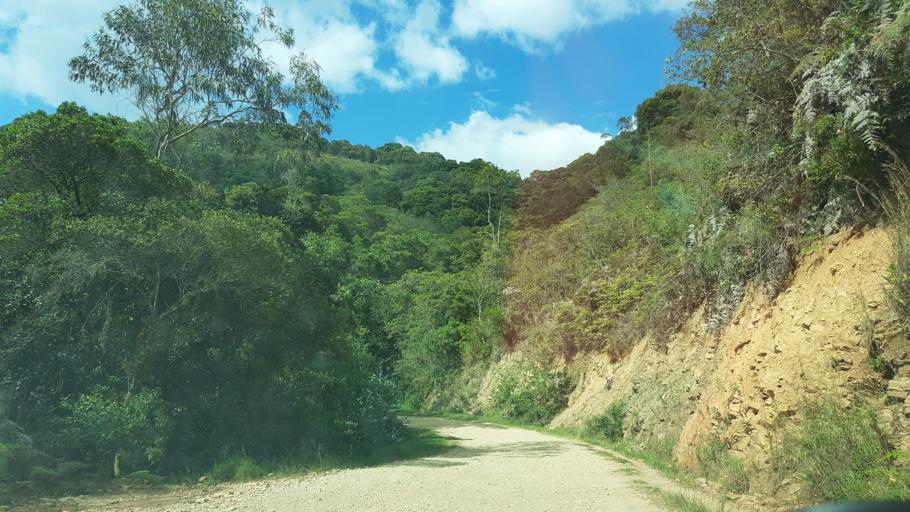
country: CO
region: Boyaca
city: Santa Sofia
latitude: 5.7245
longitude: -73.5451
